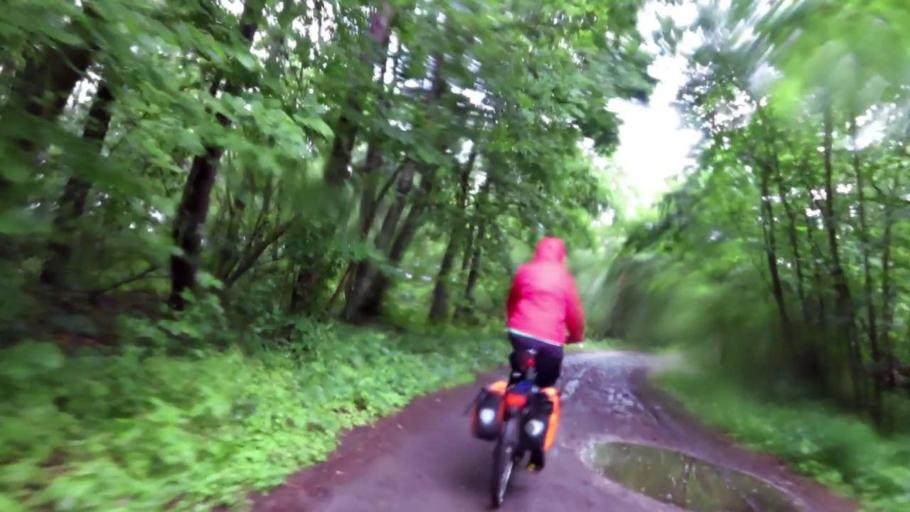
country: PL
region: West Pomeranian Voivodeship
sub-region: Powiat kolobrzeski
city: Ustronie Morskie
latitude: 54.2341
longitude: 15.8222
